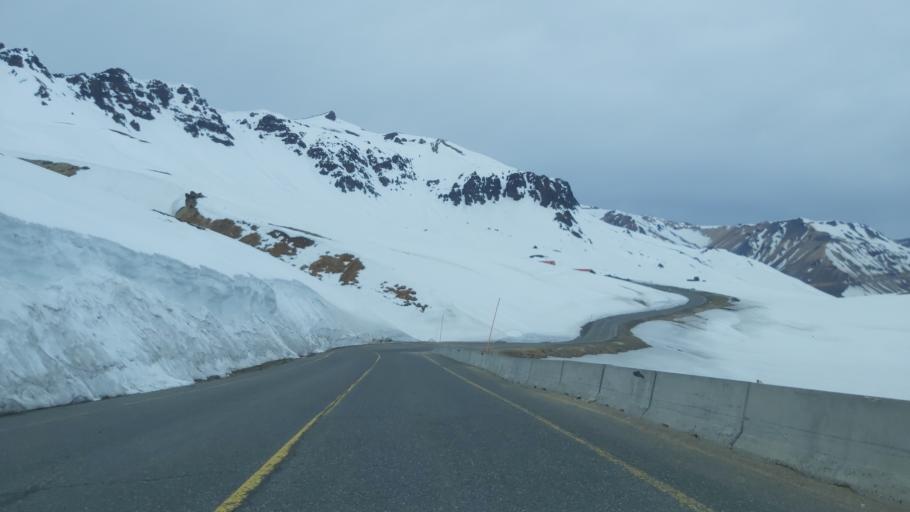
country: CL
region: Maule
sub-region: Provincia de Linares
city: Colbun
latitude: -36.0146
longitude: -70.4895
